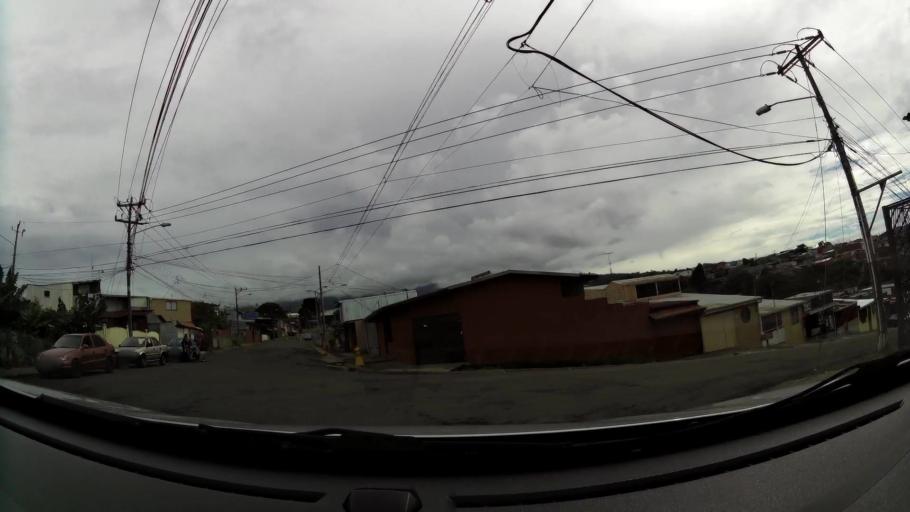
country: CR
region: San Jose
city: Ipis
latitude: 9.9653
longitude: -84.0074
